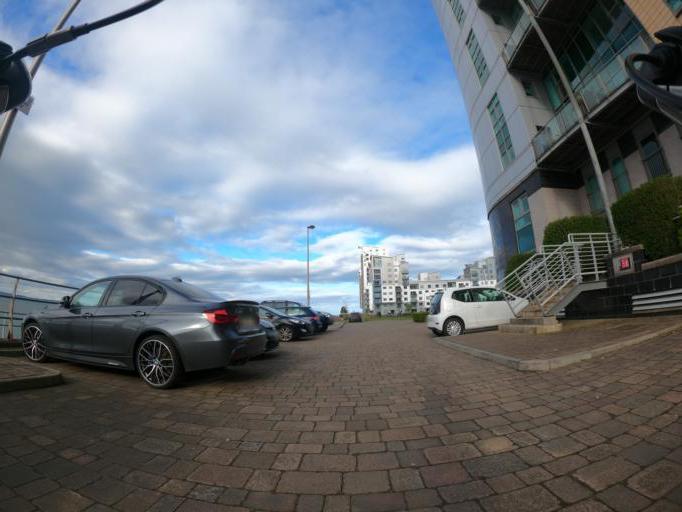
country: GB
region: Scotland
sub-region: Edinburgh
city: Edinburgh
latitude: 55.9856
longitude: -3.1933
